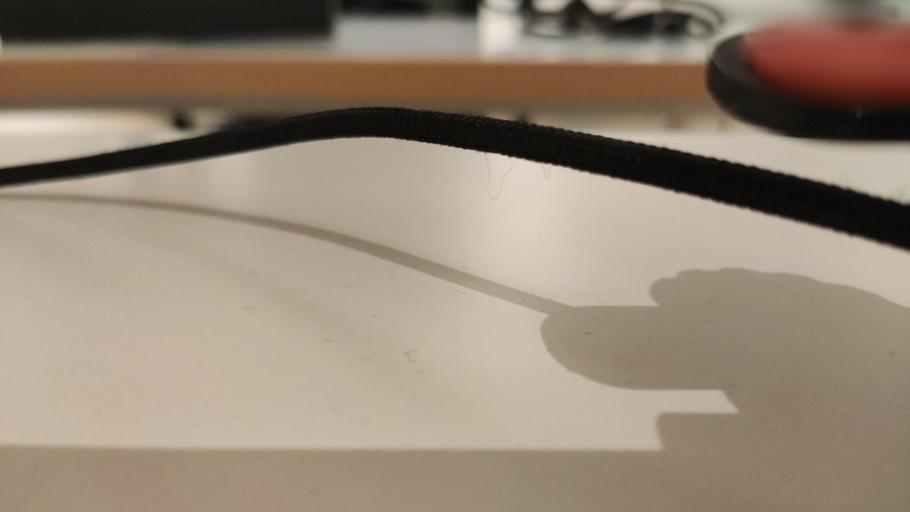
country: RU
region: Moskovskaya
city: Dorokhovo
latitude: 55.3782
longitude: 36.4040
